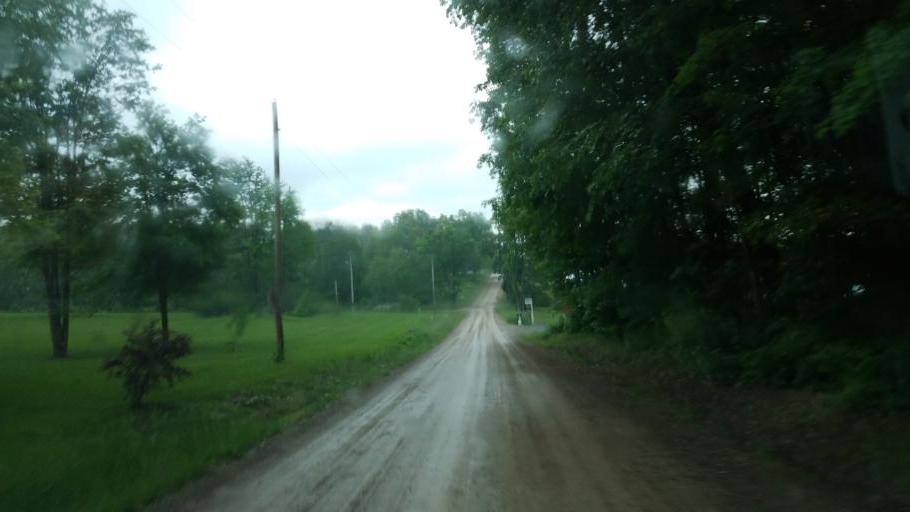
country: US
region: Ohio
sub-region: Knox County
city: Oak Hill
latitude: 40.3445
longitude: -82.2752
